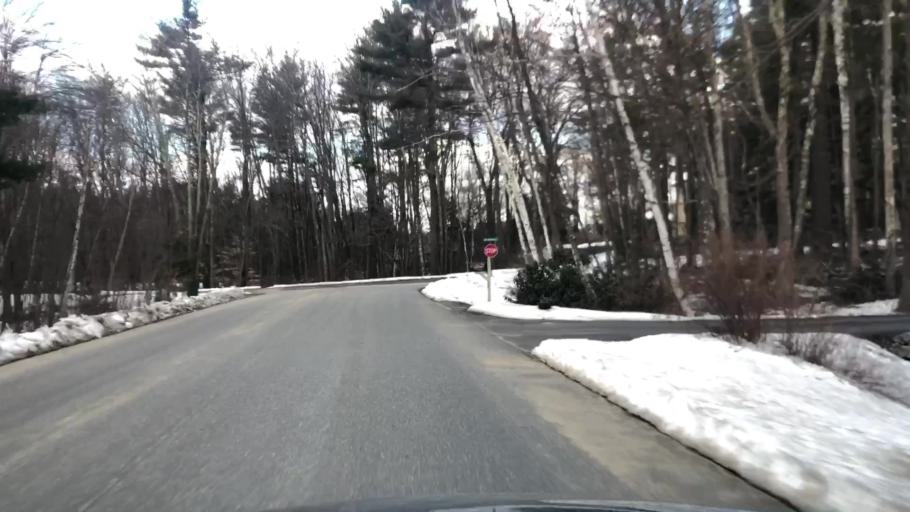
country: US
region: New Hampshire
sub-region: Hillsborough County
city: Milford
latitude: 42.8540
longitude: -71.6276
